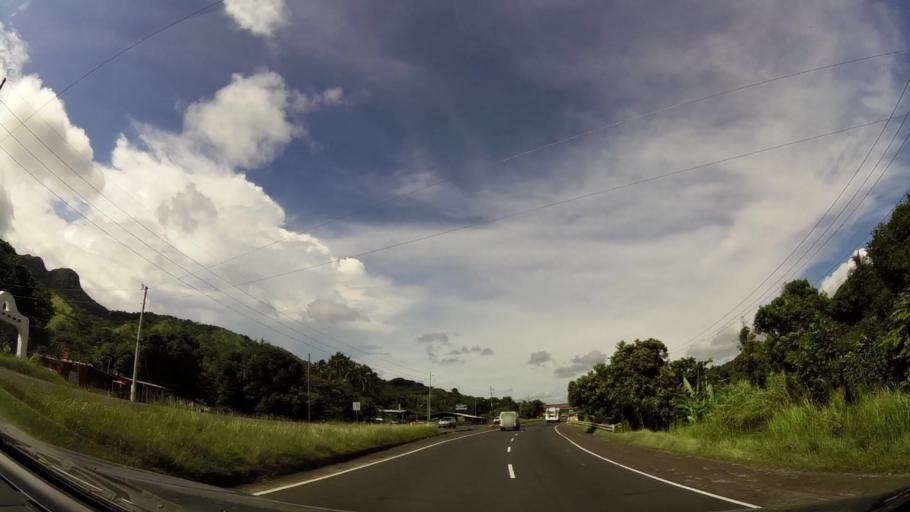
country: PA
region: Panama
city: Bejuco
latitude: 8.6600
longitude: -79.8728
